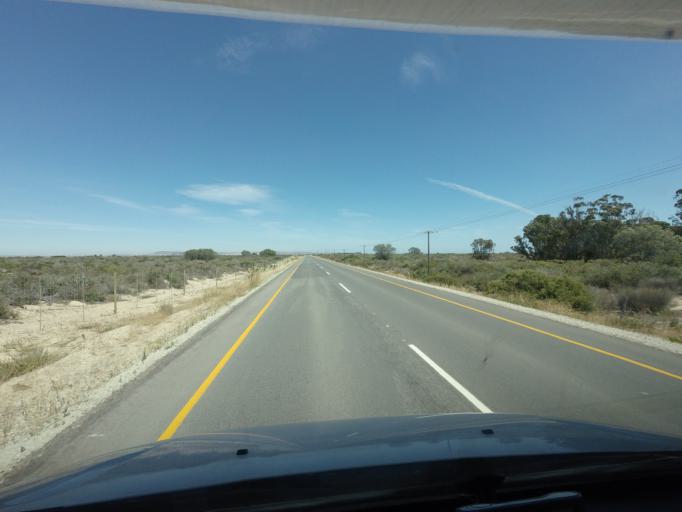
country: ZA
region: Western Cape
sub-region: West Coast District Municipality
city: Vredenburg
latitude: -32.7942
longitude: 18.2390
